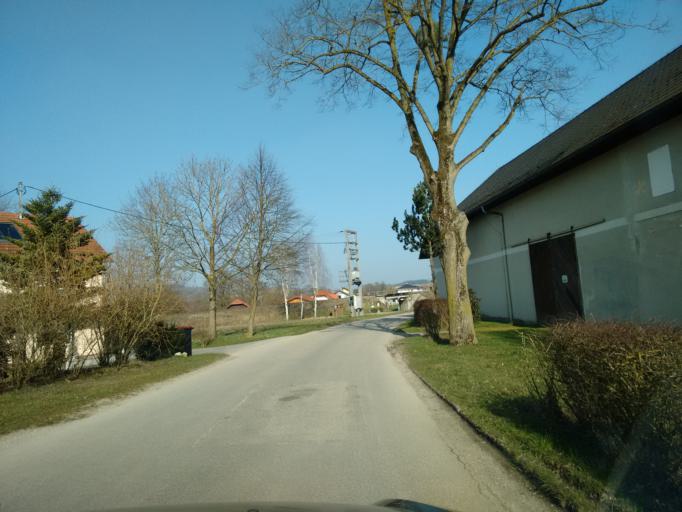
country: AT
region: Upper Austria
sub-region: Politischer Bezirk Grieskirchen
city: Bad Schallerbach
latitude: 48.2177
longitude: 13.9606
